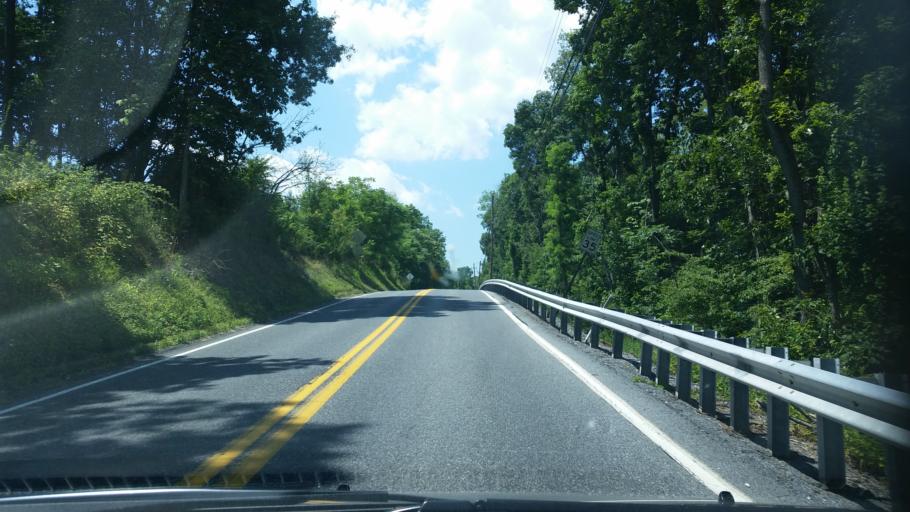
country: US
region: Pennsylvania
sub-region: Dauphin County
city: Hummelstown
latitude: 40.2899
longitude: -76.7117
